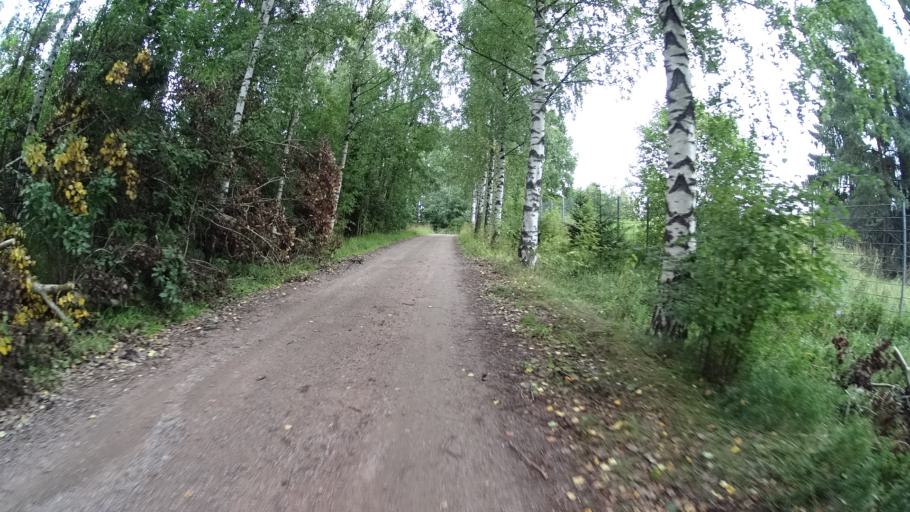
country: FI
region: Uusimaa
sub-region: Helsinki
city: Teekkarikylae
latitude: 60.2750
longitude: 24.8875
